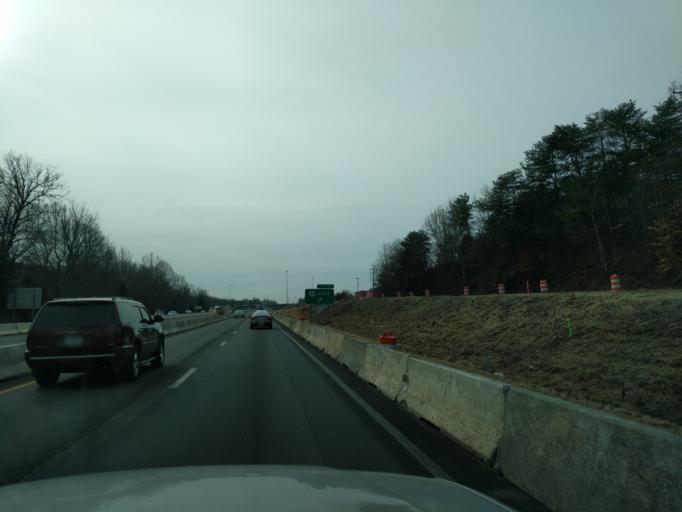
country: US
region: North Carolina
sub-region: Iredell County
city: Mooresville
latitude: 35.5596
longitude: -80.8587
